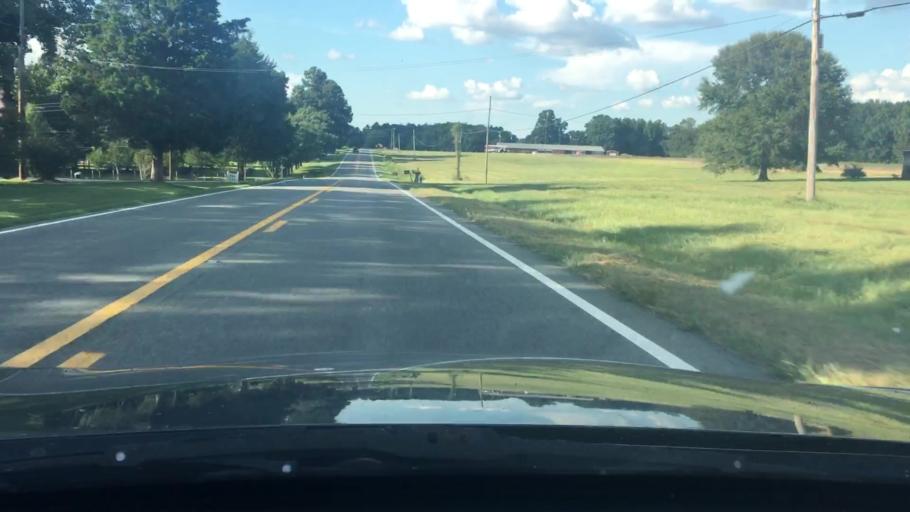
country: US
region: North Carolina
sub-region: Alamance County
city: Green Level
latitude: 36.1831
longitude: -79.3285
